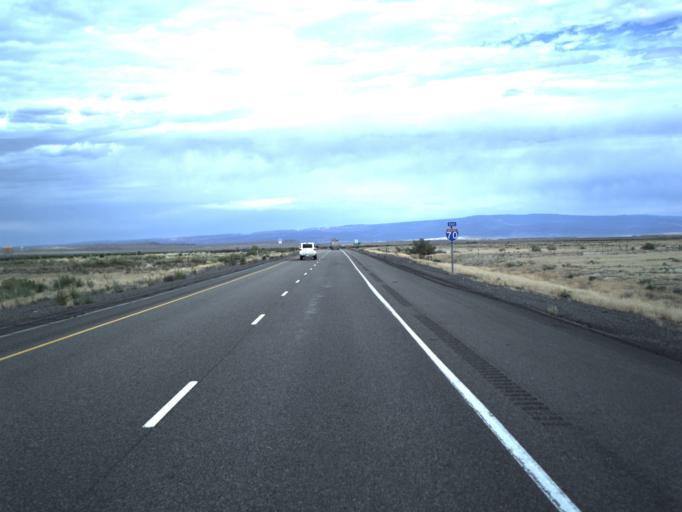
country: US
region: Utah
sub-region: Grand County
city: Moab
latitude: 38.9418
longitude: -109.6047
